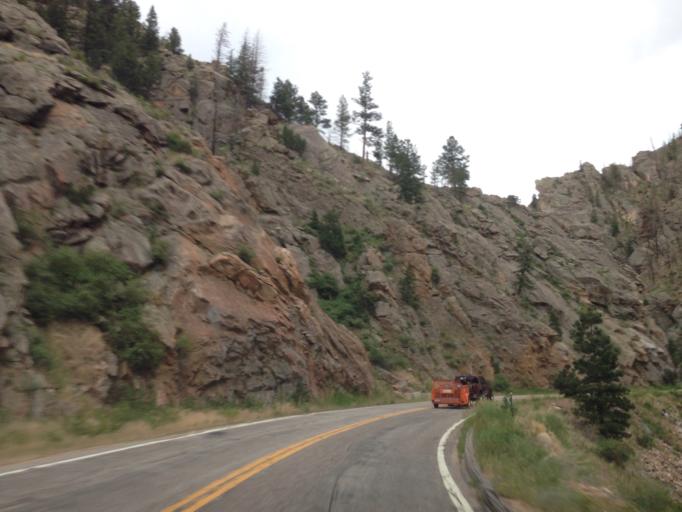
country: US
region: Colorado
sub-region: Larimer County
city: Laporte
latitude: 40.6801
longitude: -105.4332
